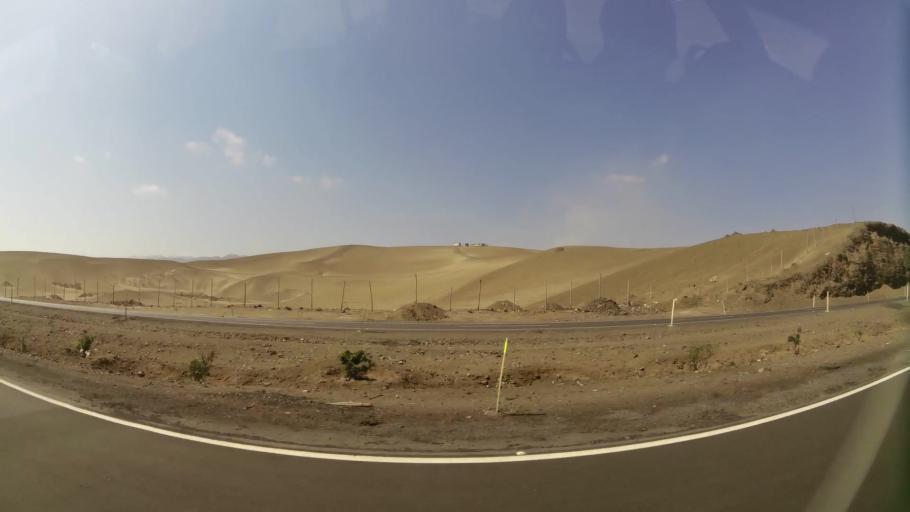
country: PE
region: Lima
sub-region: Provincia de Canete
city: Quilmana
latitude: -12.9342
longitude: -76.4985
